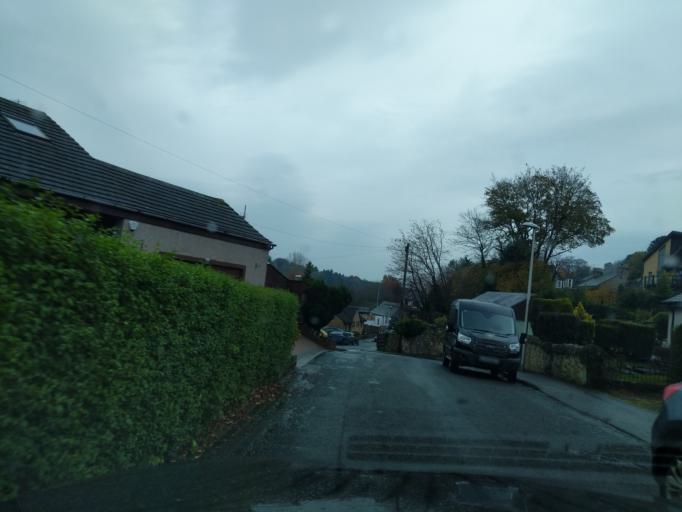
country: GB
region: Scotland
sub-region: Midlothian
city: Bonnyrigg
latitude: 55.8814
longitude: -3.1157
